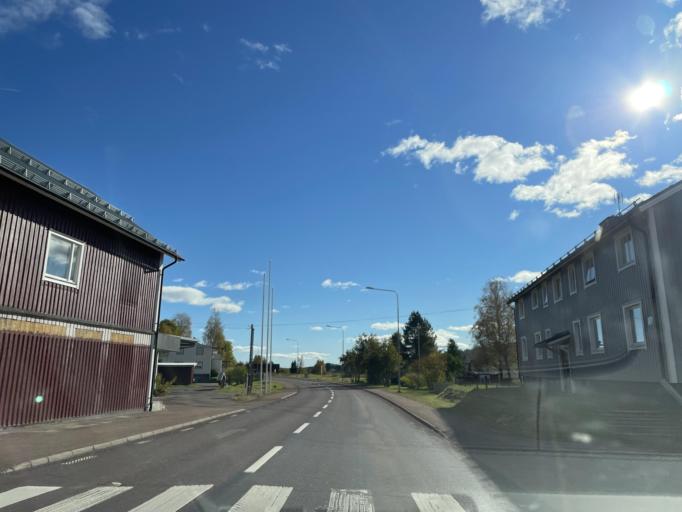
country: SE
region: Dalarna
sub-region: Malung-Saelens kommun
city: Malung
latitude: 60.9810
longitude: 13.3356
